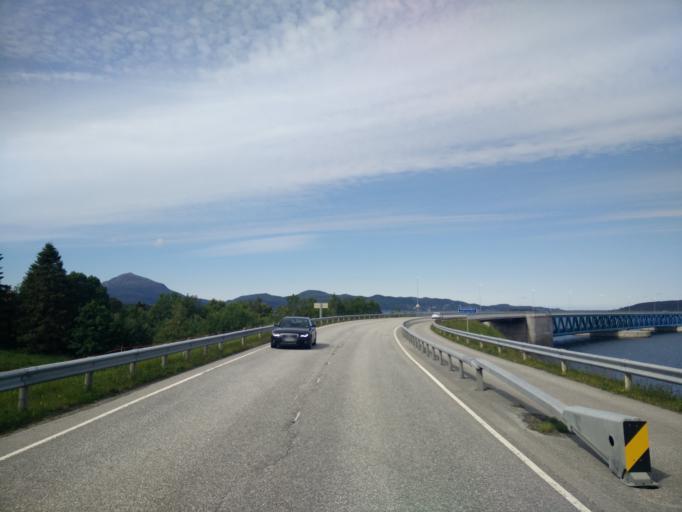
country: NO
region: More og Romsdal
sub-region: Kristiansund
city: Rensvik
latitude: 62.9820
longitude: 7.8698
